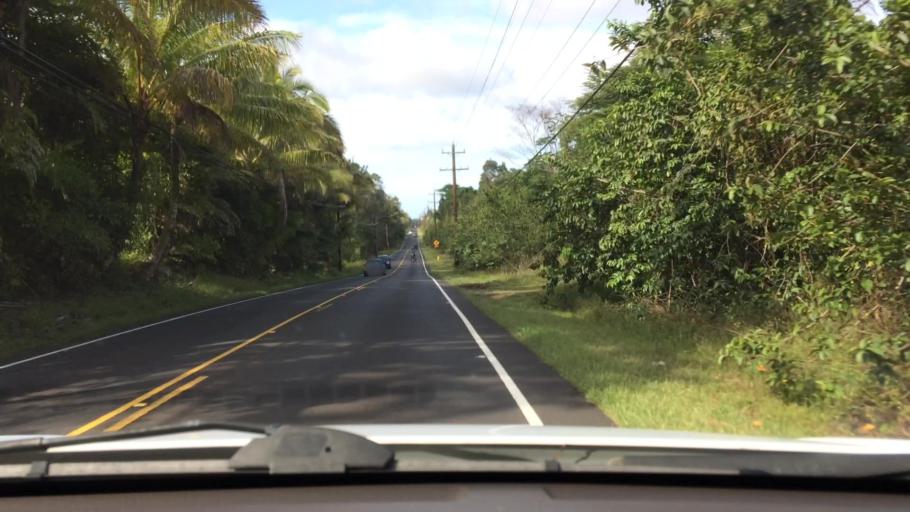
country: US
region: Hawaii
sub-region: Hawaii County
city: Hawaiian Paradise Park
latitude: 19.5119
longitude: -154.9431
